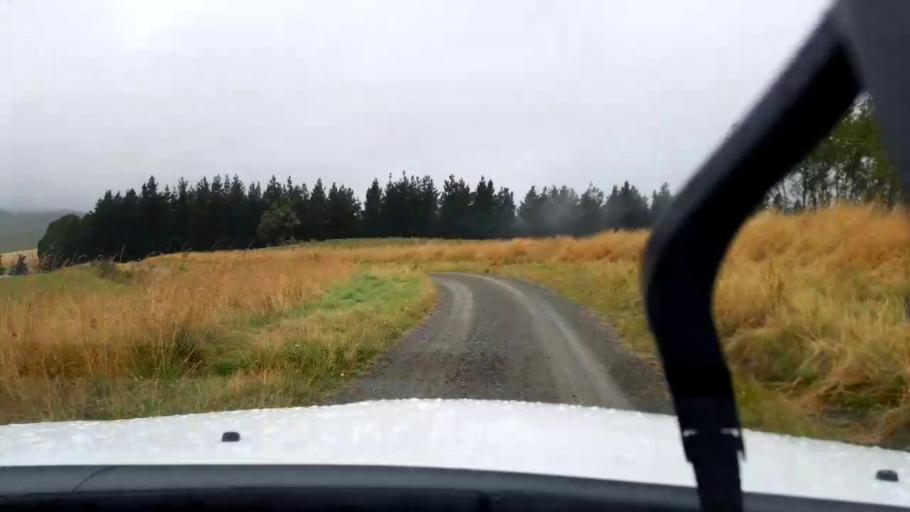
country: NZ
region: Canterbury
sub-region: Timaru District
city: Pleasant Point
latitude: -44.1775
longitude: 171.0924
